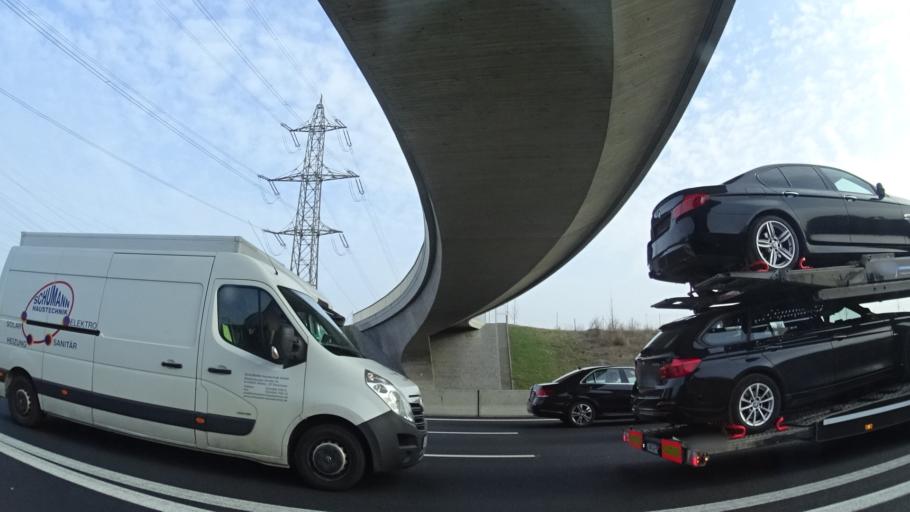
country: DE
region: Baden-Wuerttemberg
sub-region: Regierungsbezirk Stuttgart
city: Rutesheim
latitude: 48.7890
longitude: 8.9778
